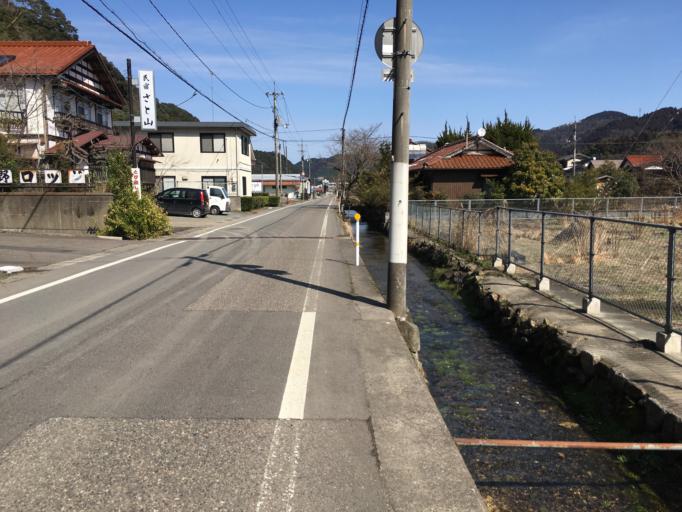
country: JP
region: Shimane
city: Masuda
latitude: 34.4560
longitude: 131.7661
